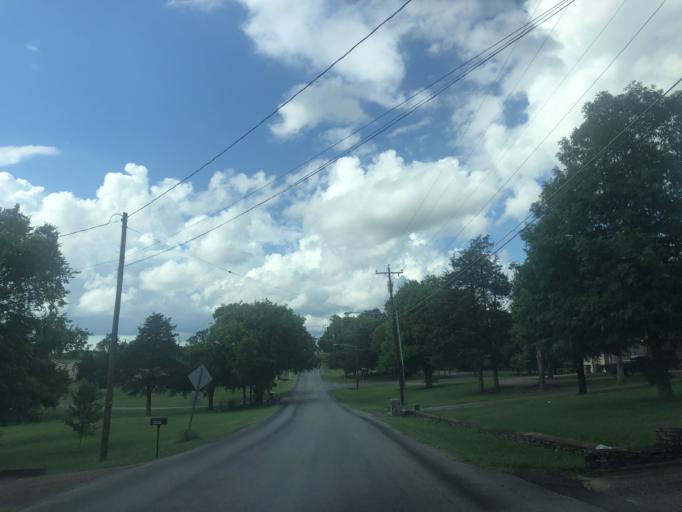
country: US
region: Tennessee
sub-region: Davidson County
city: Nashville
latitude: 36.2111
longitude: -86.8584
